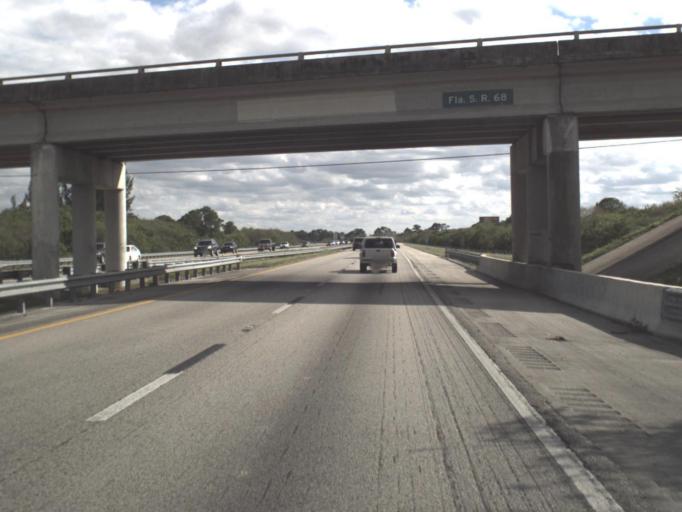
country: US
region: Florida
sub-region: Saint Lucie County
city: Lakewood Park
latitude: 27.4479
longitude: -80.4275
